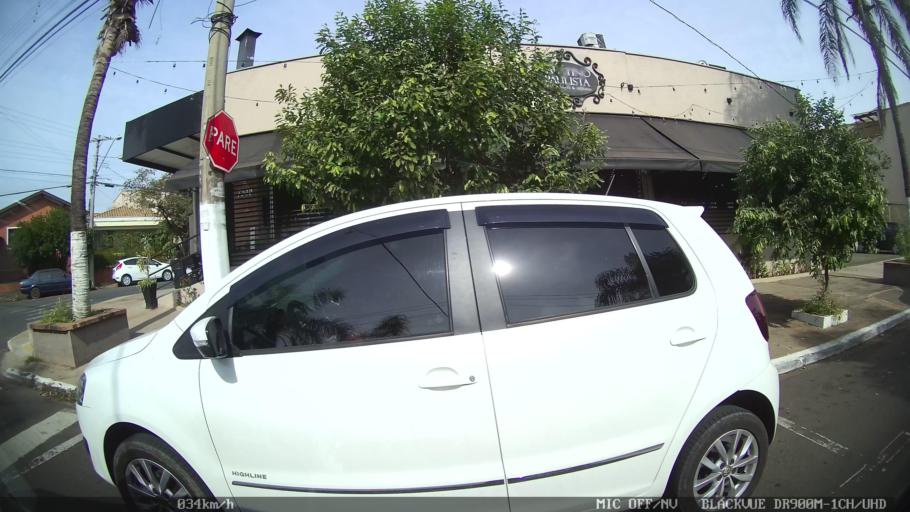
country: BR
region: Sao Paulo
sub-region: Piracicaba
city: Piracicaba
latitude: -22.7352
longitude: -47.6618
